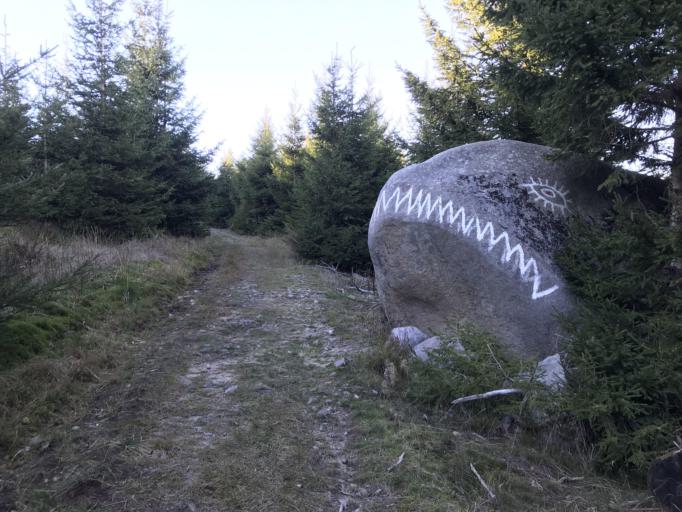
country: DE
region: Saxony-Anhalt
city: Darlingerode
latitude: 51.7909
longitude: 10.6816
